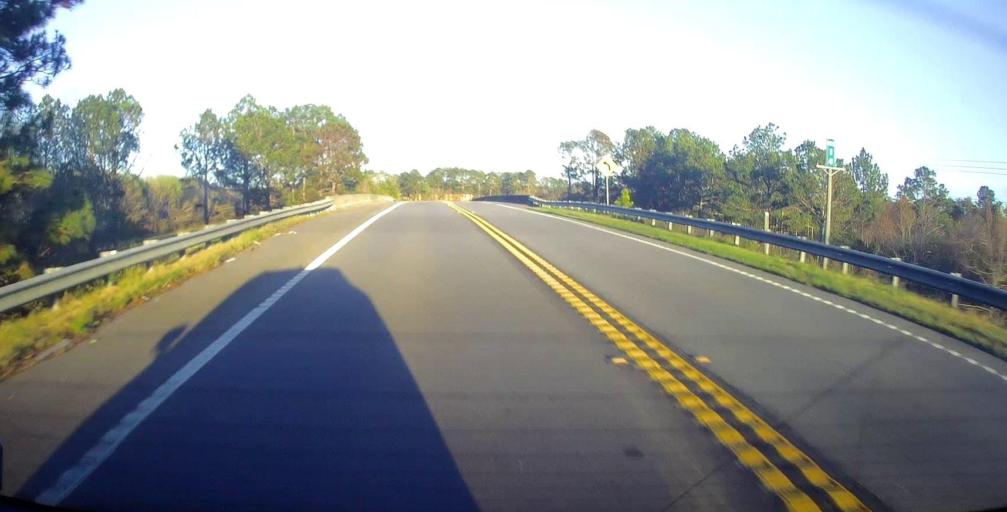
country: US
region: Georgia
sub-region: Crisp County
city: Cordele
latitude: 31.9501
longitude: -83.7042
